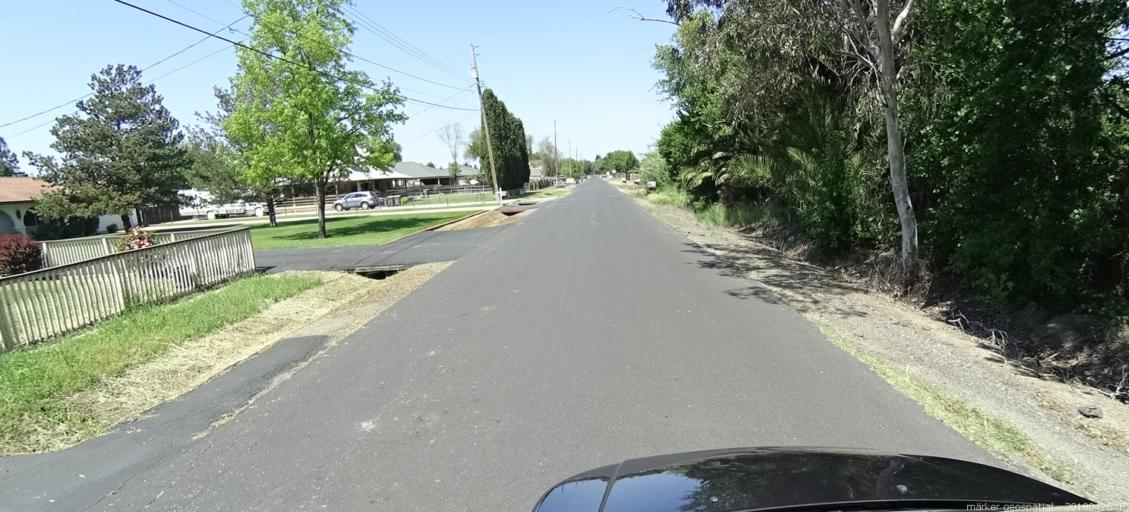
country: US
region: California
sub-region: Yolo County
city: West Sacramento
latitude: 38.5425
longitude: -121.5502
